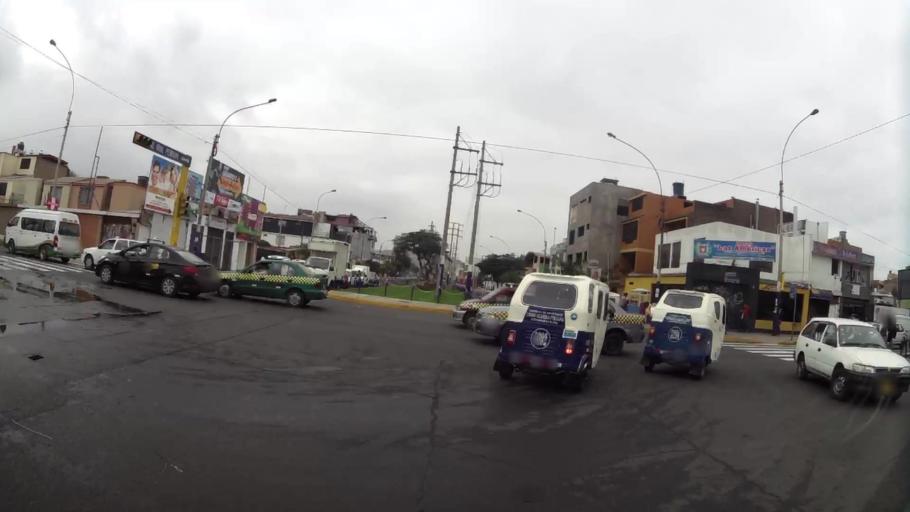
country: PE
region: Lima
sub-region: Lima
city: Surco
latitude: -12.1764
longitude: -77.0070
